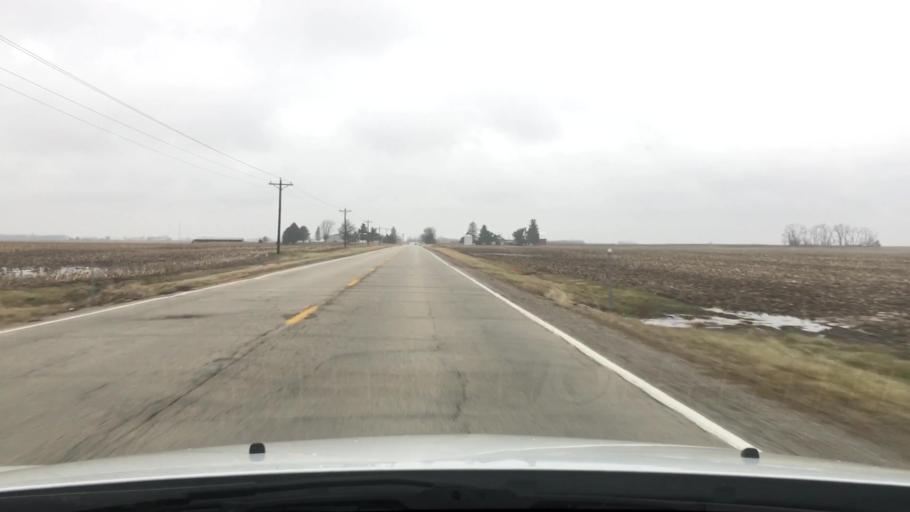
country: US
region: Illinois
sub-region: Iroquois County
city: Watseka
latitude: 40.8905
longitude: -87.6984
